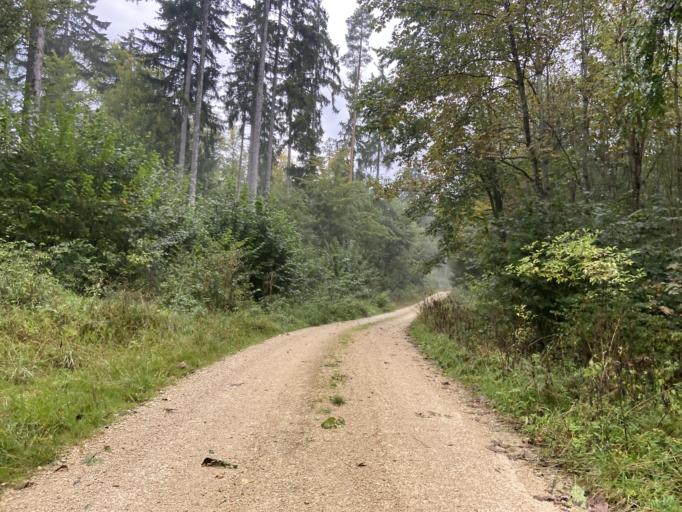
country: DE
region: Baden-Wuerttemberg
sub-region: Tuebingen Region
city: Bingen
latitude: 48.1237
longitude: 9.2713
